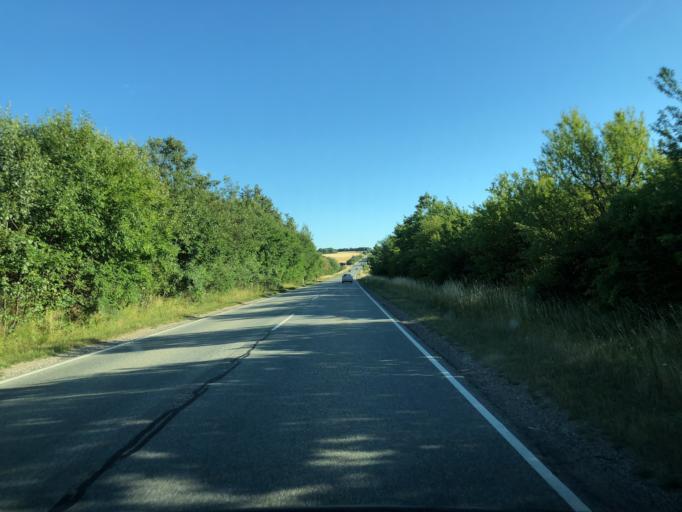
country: DK
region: Central Jutland
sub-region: Arhus Kommune
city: Framlev
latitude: 56.1303
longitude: 9.9960
